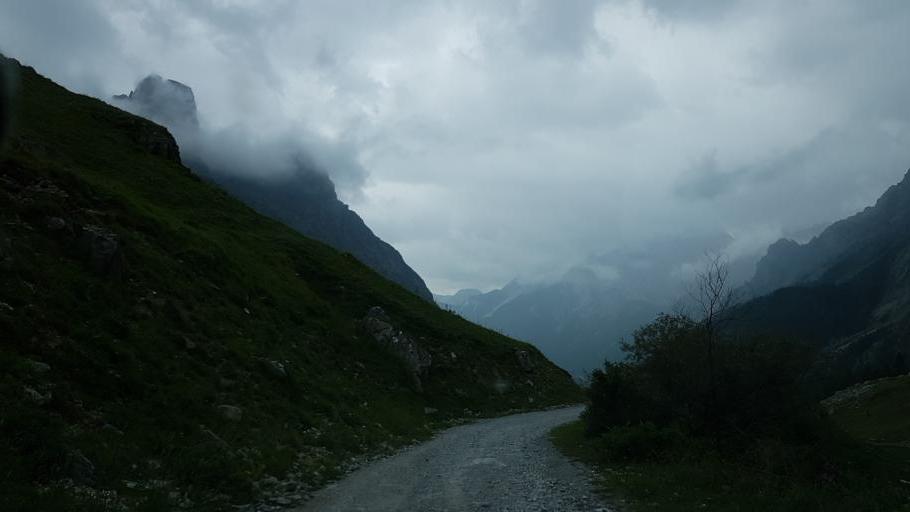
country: IT
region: Piedmont
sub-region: Provincia di Cuneo
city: Acceglio
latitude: 44.5200
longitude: 6.9053
